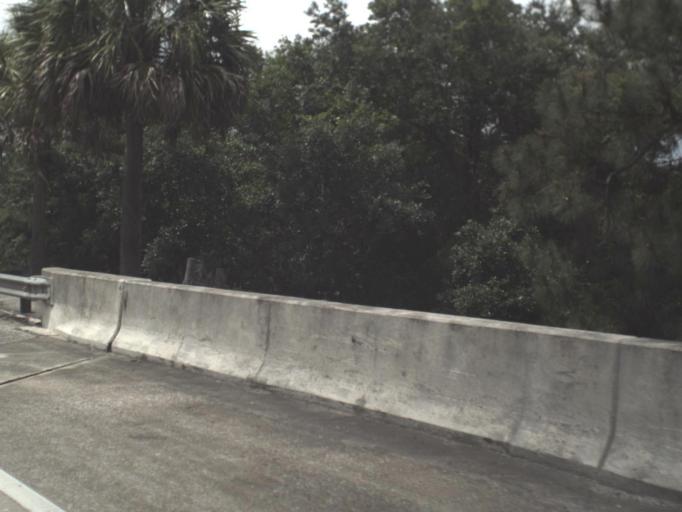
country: US
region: Florida
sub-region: Flagler County
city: Palm Coast
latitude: 29.6725
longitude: -81.3051
